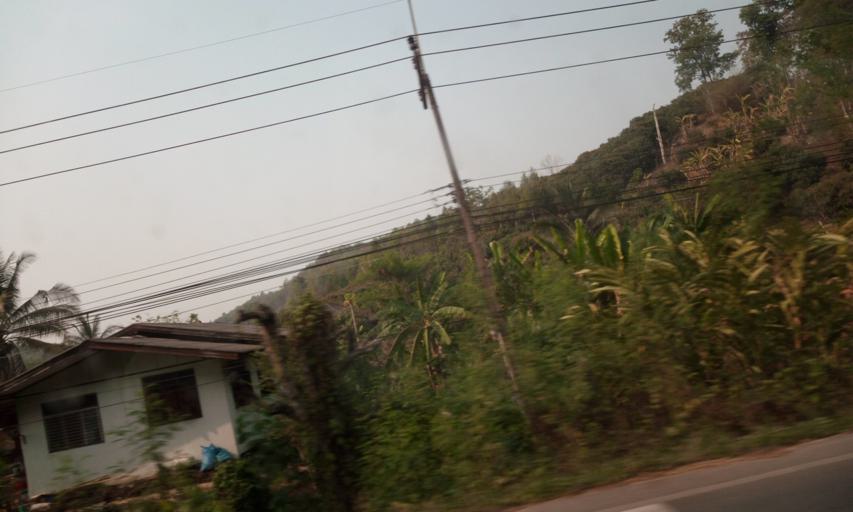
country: TH
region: Chiang Rai
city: Pa Daet
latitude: 19.6161
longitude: 99.9978
